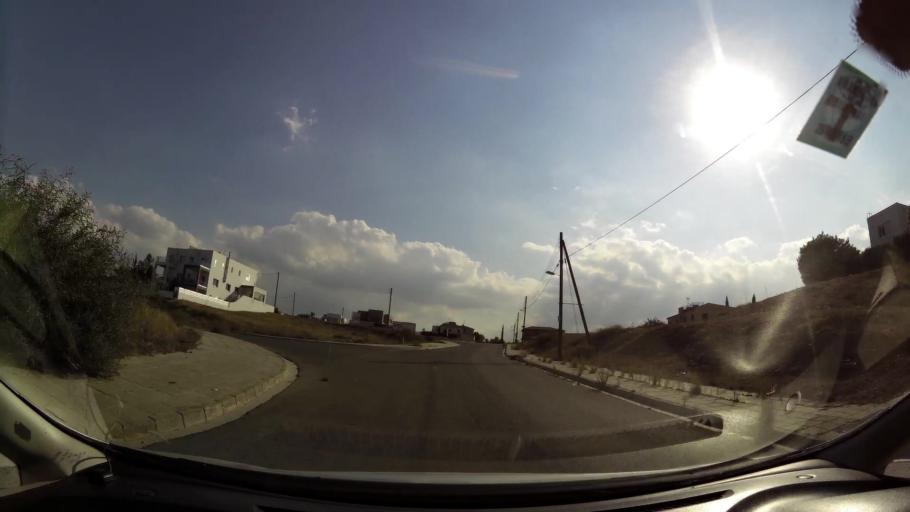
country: CY
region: Lefkosia
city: Kato Deftera
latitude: 35.1418
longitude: 33.2949
